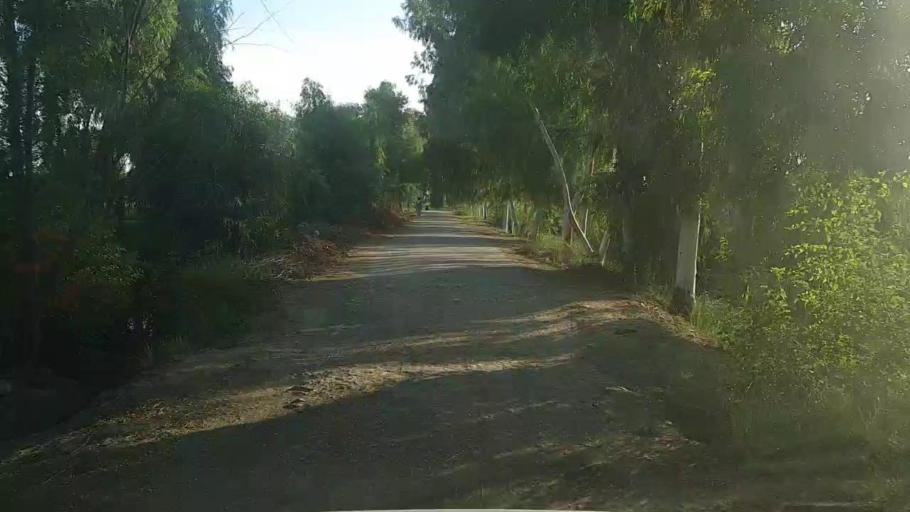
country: PK
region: Sindh
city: Khairpur
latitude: 28.0841
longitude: 69.6370
